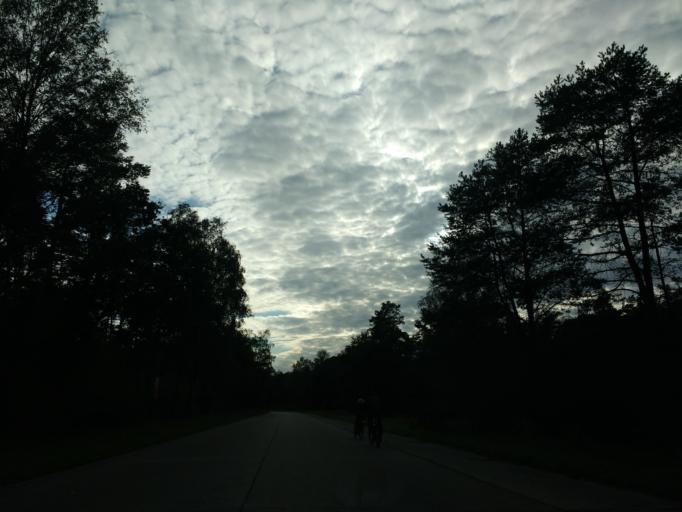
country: DE
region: North Rhine-Westphalia
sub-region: Regierungsbezirk Detmold
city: Augustdorf
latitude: 51.8761
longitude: 8.7067
